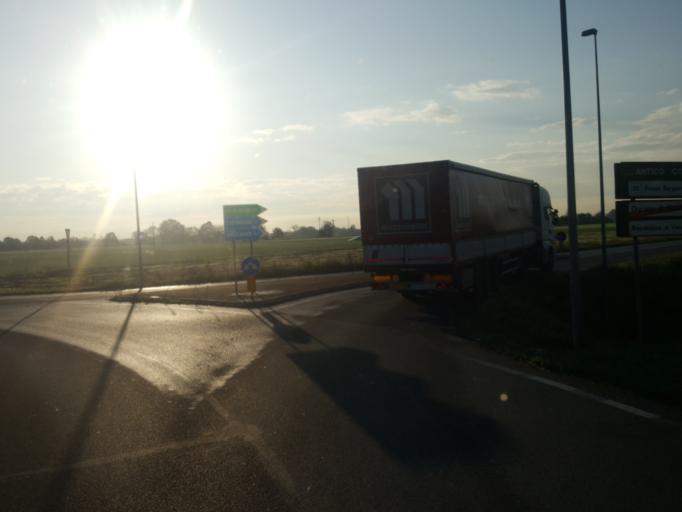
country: IT
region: Lombardy
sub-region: Provincia di Bergamo
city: Morengo
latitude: 45.5329
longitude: 9.6890
